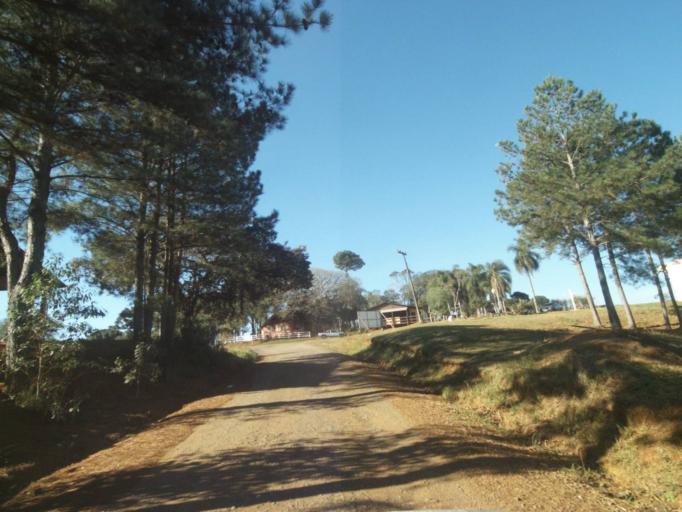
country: BR
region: Parana
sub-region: Tibagi
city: Tibagi
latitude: -24.5409
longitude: -50.4987
